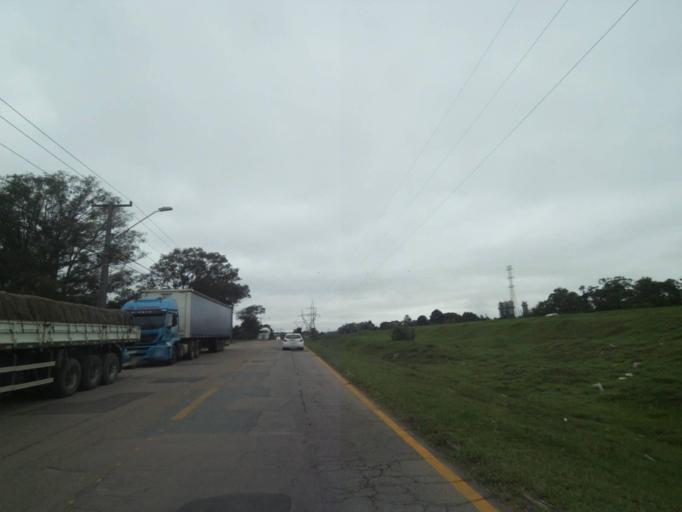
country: BR
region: Parana
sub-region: Araucaria
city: Araucaria
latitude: -25.5483
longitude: -49.3238
